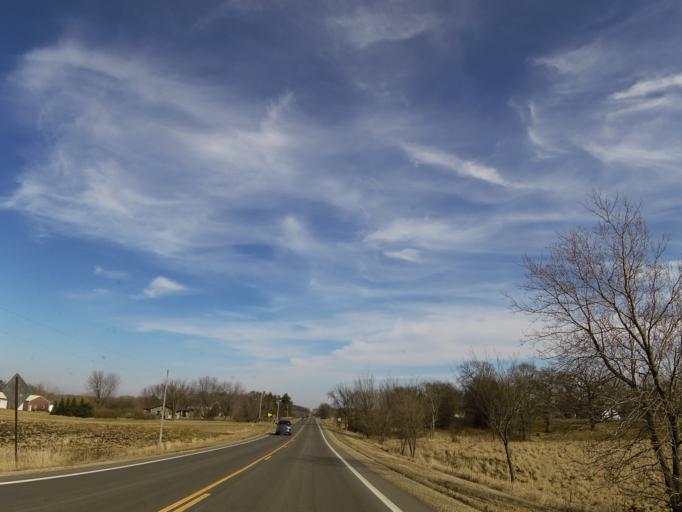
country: US
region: Minnesota
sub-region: Scott County
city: Elko New Market
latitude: 44.5440
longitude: -93.3113
